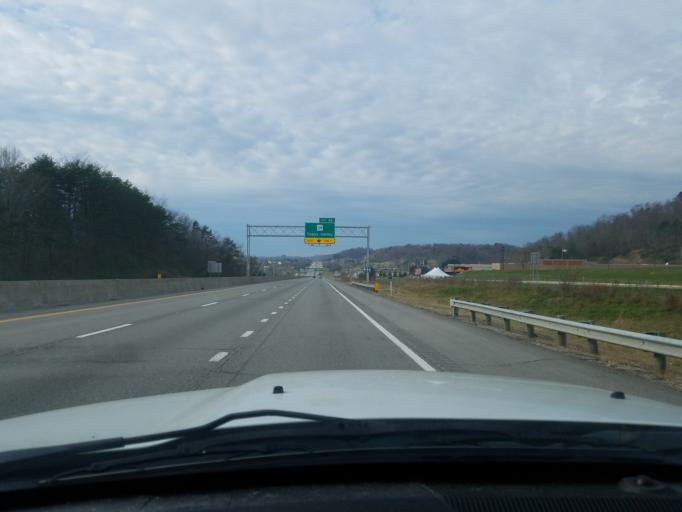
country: US
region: West Virginia
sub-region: Putnam County
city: Teays Valley
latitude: 38.4548
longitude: -81.9213
